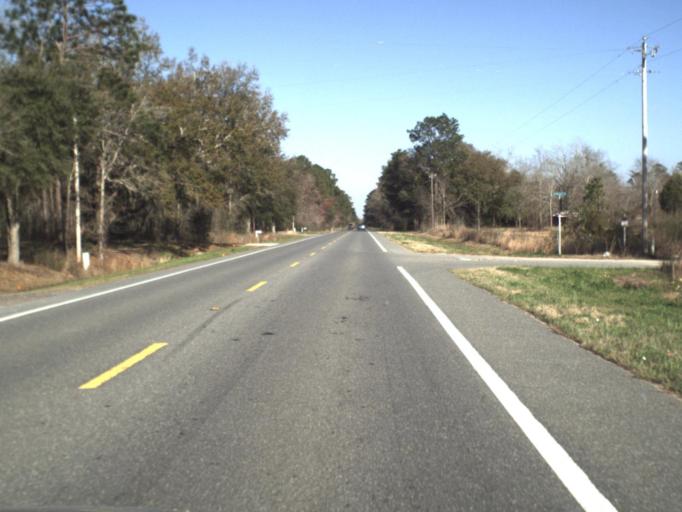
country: US
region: Florida
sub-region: Washington County
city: Chipley
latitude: 30.7900
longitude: -85.4072
